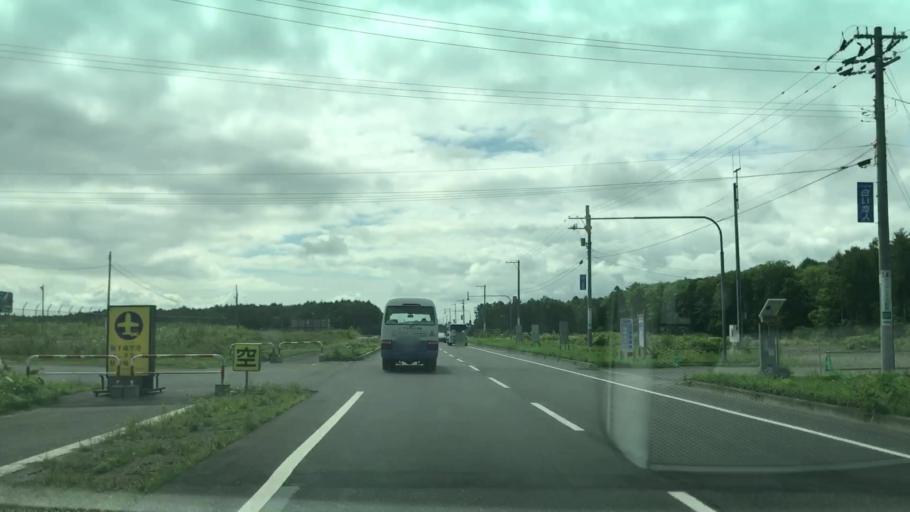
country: JP
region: Hokkaido
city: Chitose
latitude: 42.7722
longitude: 141.6790
